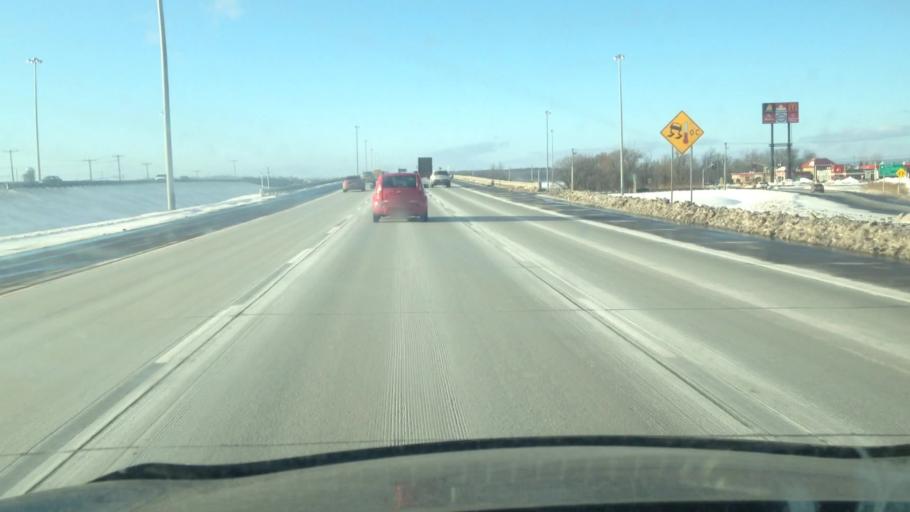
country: CA
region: Quebec
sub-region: Laurentides
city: Blainville
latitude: 45.6913
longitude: -73.9347
